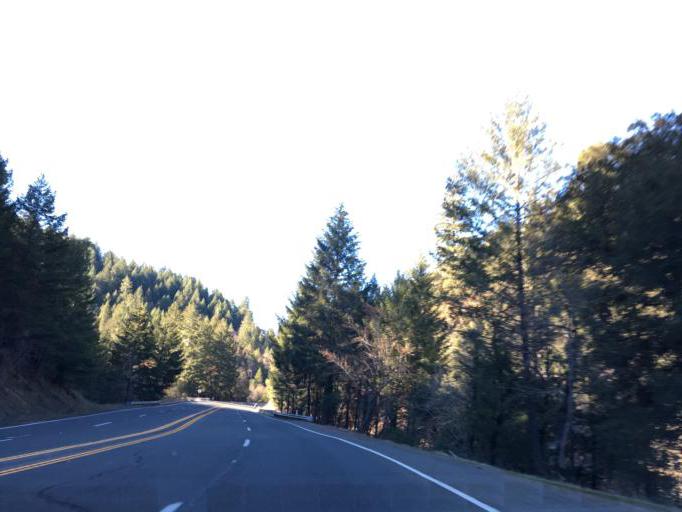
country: US
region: California
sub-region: Mendocino County
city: Laytonville
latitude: 39.6084
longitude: -123.4569
